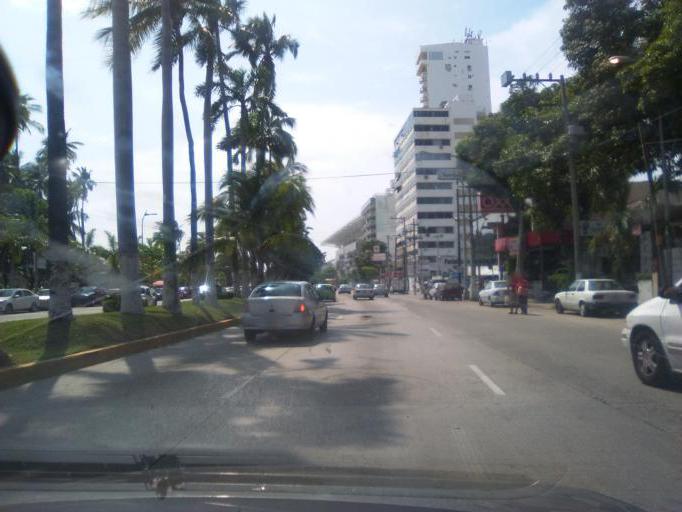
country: MX
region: Guerrero
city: Acapulco de Juarez
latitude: 16.8567
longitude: -99.8943
